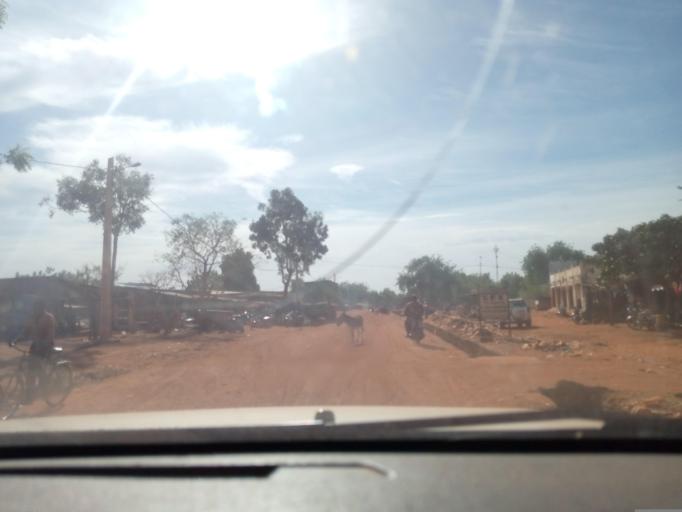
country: ML
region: Sikasso
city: Sikasso
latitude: 11.8541
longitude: -6.0179
